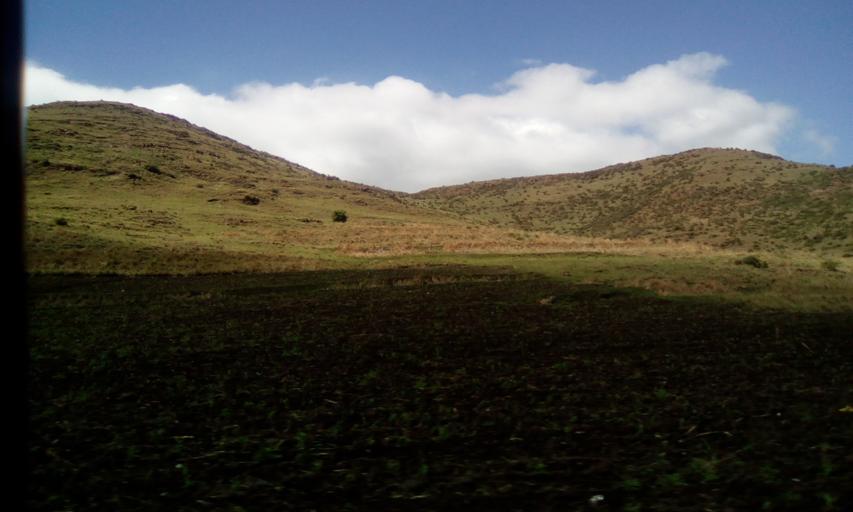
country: LS
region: Maseru
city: Nako
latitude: -29.6565
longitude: 27.8540
